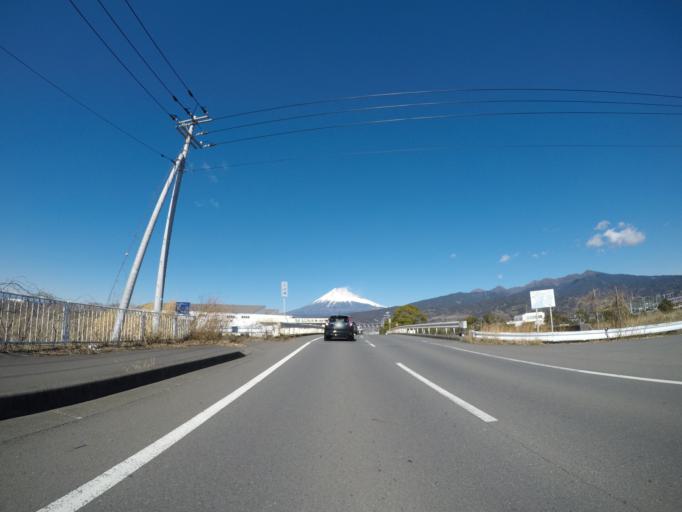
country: JP
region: Shizuoka
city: Fuji
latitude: 35.1428
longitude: 138.7407
